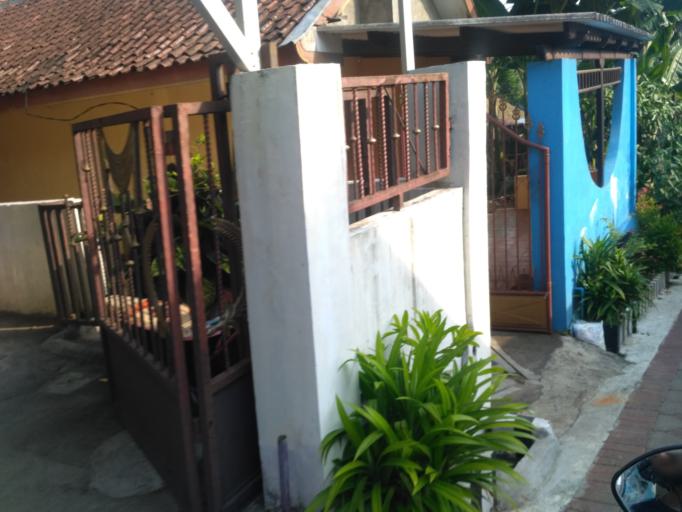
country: ID
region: East Java
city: Malang
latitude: -7.9571
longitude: 112.6251
